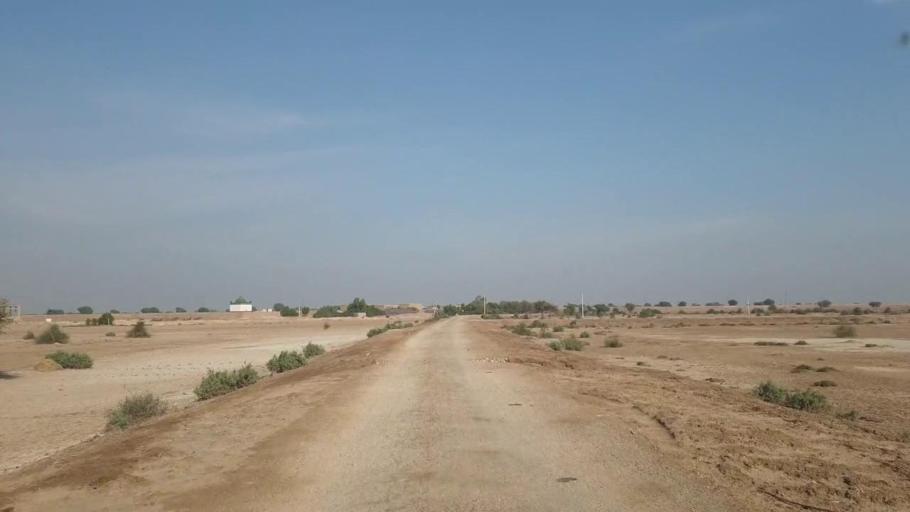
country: PK
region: Sindh
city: Sann
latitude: 25.9256
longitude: 68.2174
